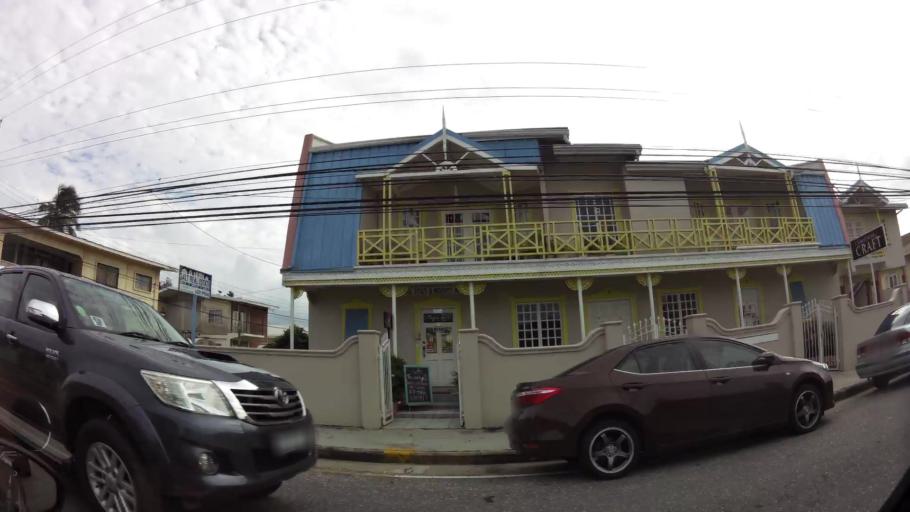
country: TT
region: City of Port of Spain
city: Port-of-Spain
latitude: 10.6656
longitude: -61.5257
